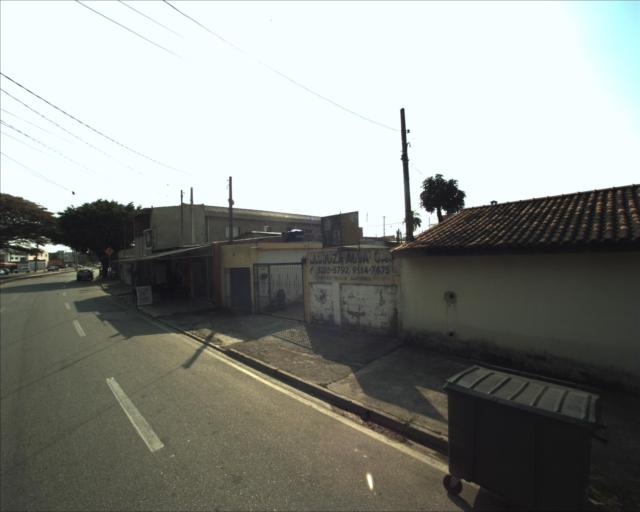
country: BR
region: Sao Paulo
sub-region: Sorocaba
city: Sorocaba
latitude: -23.4333
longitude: -47.4558
